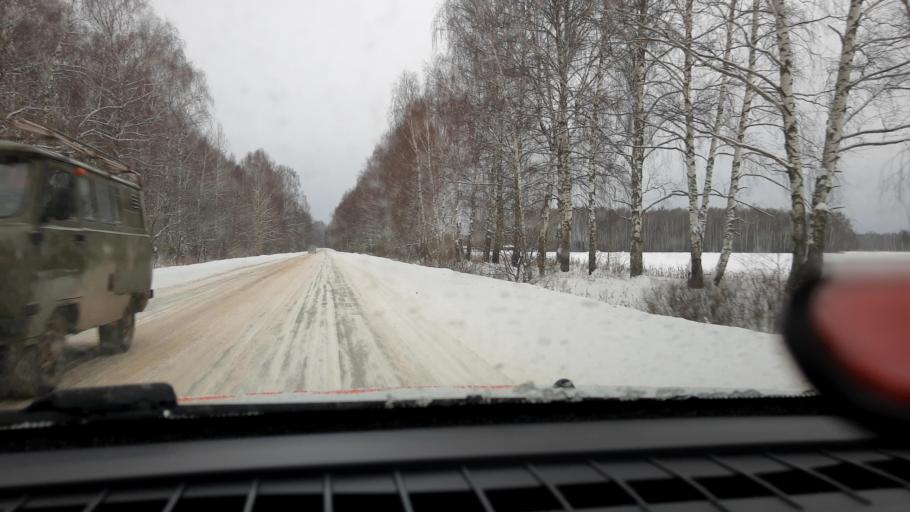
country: RU
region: Nizjnij Novgorod
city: Pamyat' Parizhskoy Kommuny
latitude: 56.2518
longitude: 44.4749
